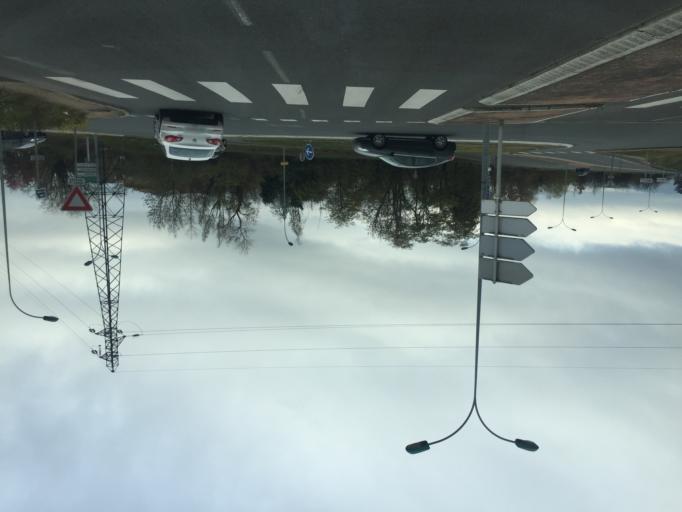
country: FR
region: Rhone-Alpes
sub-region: Departement de l'Ain
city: Jassans-Riottier
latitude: 45.9980
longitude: 4.7396
